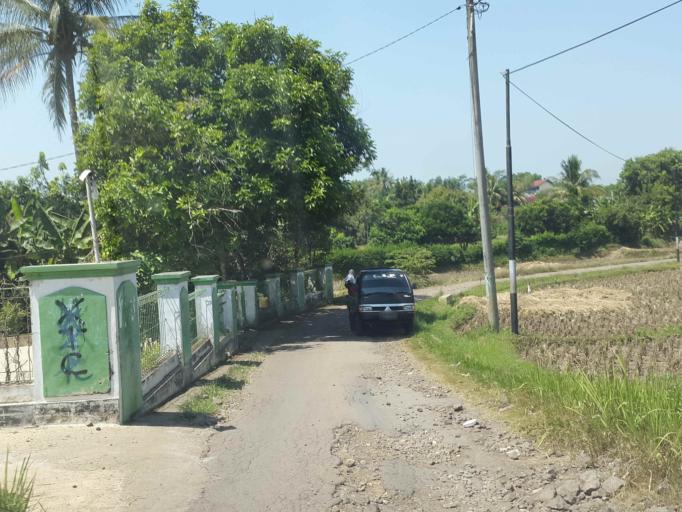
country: ID
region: West Java
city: Ciranjang-hilir
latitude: -6.7929
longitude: 107.2820
